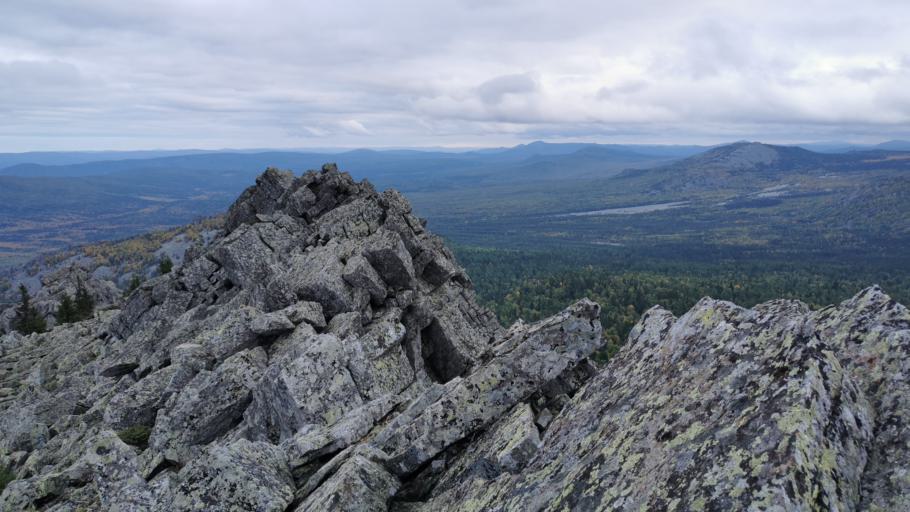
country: RU
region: Bashkortostan
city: Tirlyanskiy
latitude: 54.3773
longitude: 58.4194
